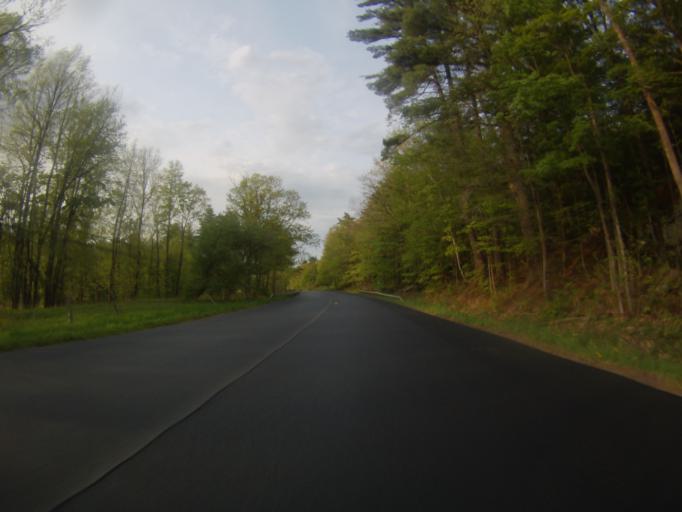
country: US
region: New York
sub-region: Essex County
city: Ticonderoga
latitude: 43.8312
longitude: -73.4638
